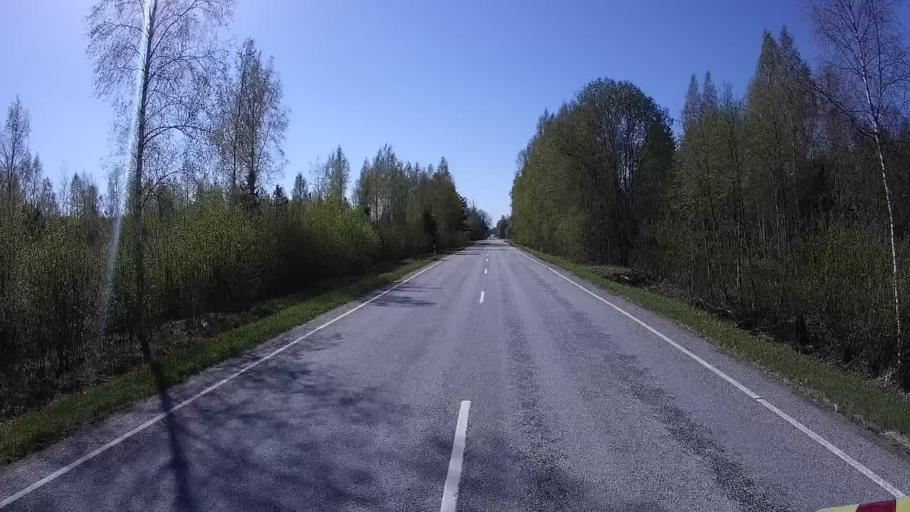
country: EE
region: Raplamaa
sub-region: Jaervakandi vald
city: Jarvakandi
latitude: 58.8057
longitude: 24.8105
